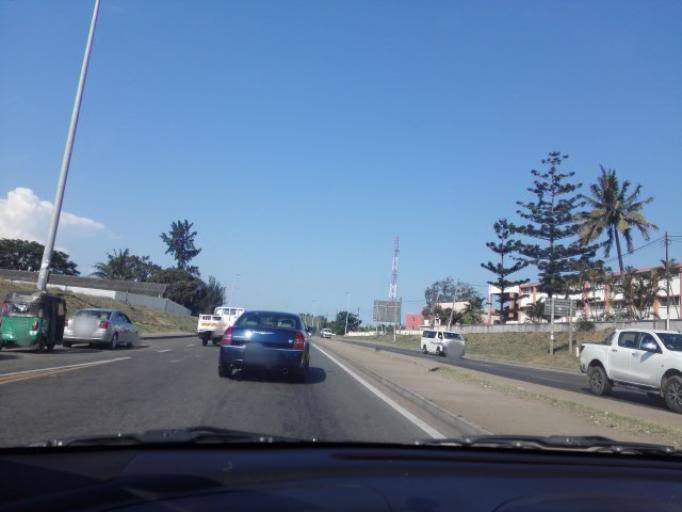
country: MZ
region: Maputo City
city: Maputo
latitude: -25.9432
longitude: 32.5419
